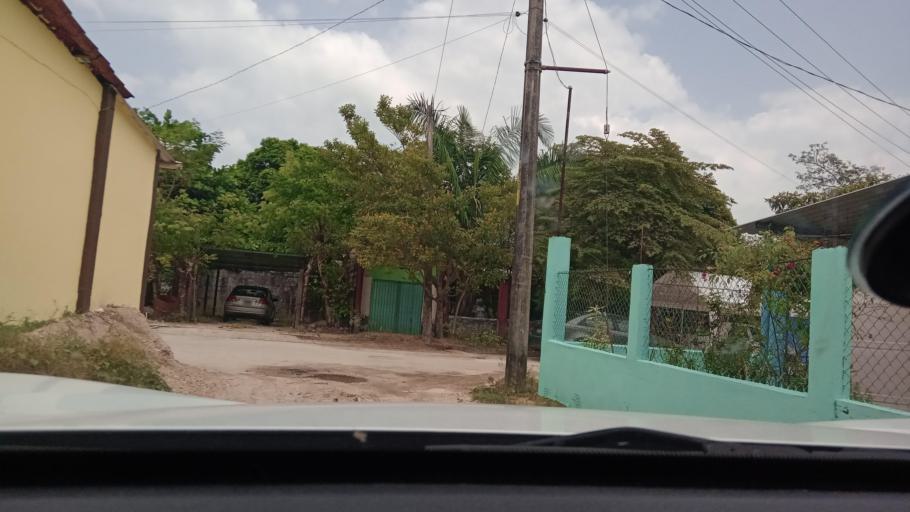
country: MX
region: Veracruz
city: Las Choapas
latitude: 17.8872
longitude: -94.1028
